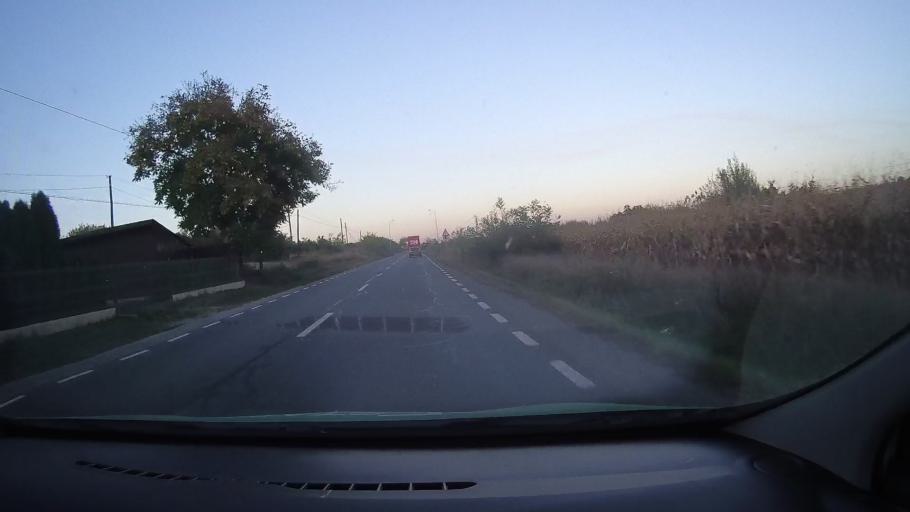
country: RO
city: Szekelyhid
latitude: 47.3637
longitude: 22.1175
